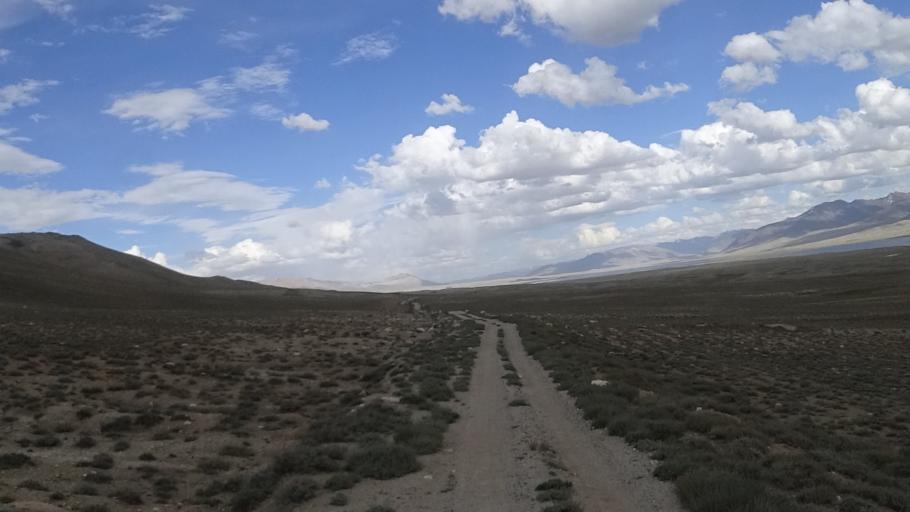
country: TJ
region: Gorno-Badakhshan
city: Murghob
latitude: 37.4679
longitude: 73.5687
